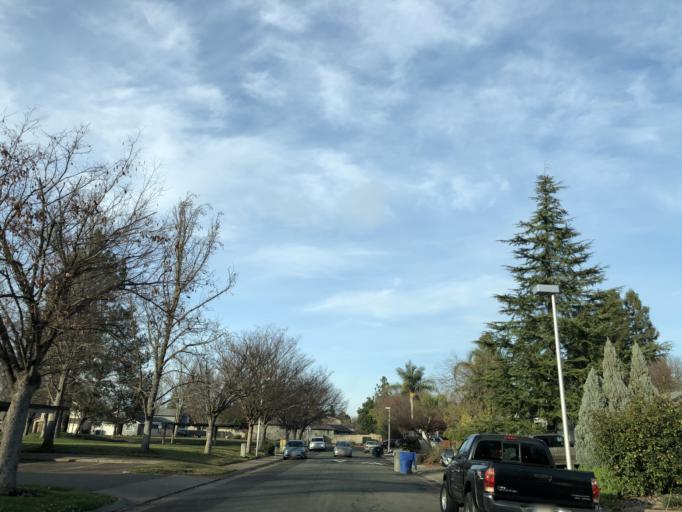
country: US
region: California
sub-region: Sacramento County
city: Parkway
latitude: 38.5484
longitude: -121.4406
